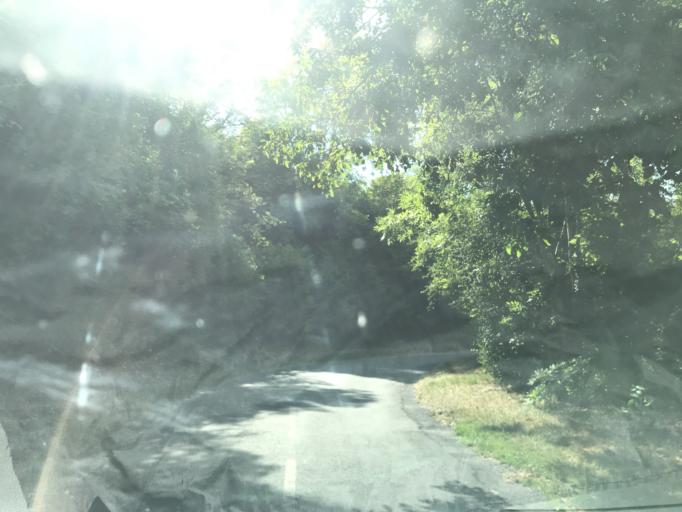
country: FR
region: Ile-de-France
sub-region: Departement des Yvelines
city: Freneuse
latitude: 49.0619
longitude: 1.5998
